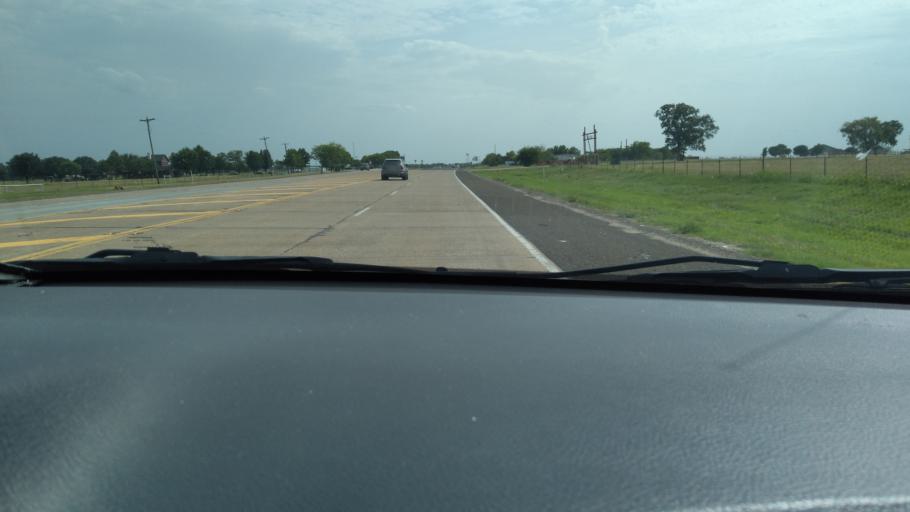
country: US
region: Texas
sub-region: Navarro County
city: Corsicana
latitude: 32.0505
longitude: -96.5340
